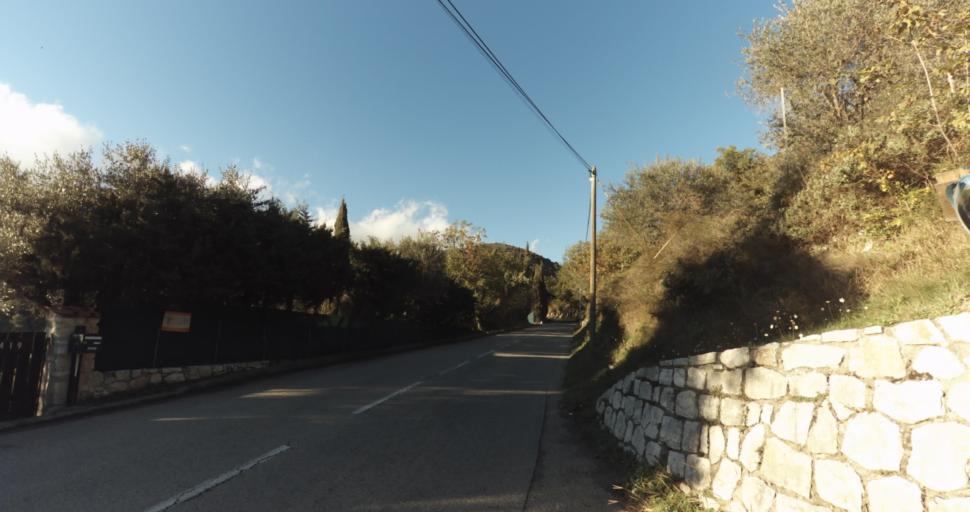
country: FR
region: Provence-Alpes-Cote d'Azur
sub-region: Departement des Alpes-Maritimes
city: Vence
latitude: 43.7328
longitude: 7.1059
